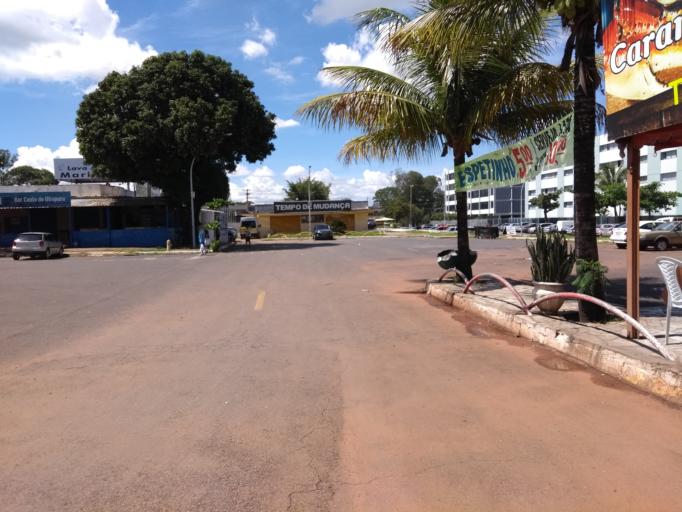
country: BR
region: Federal District
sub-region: Brasilia
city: Brasilia
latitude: -15.7982
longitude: -47.9357
